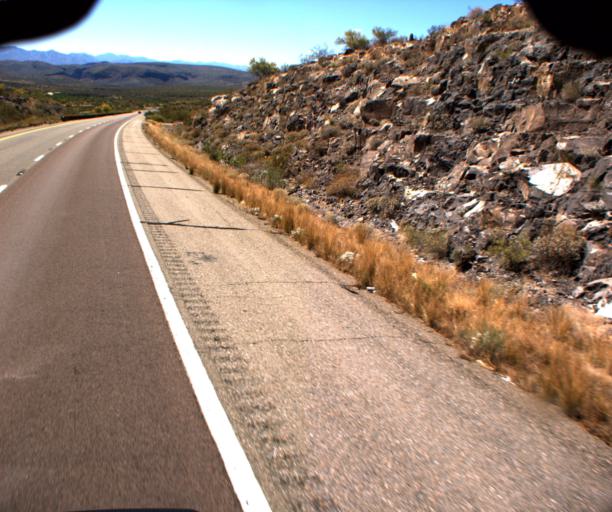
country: US
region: Arizona
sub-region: Yavapai County
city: Bagdad
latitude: 34.5037
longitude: -113.4069
